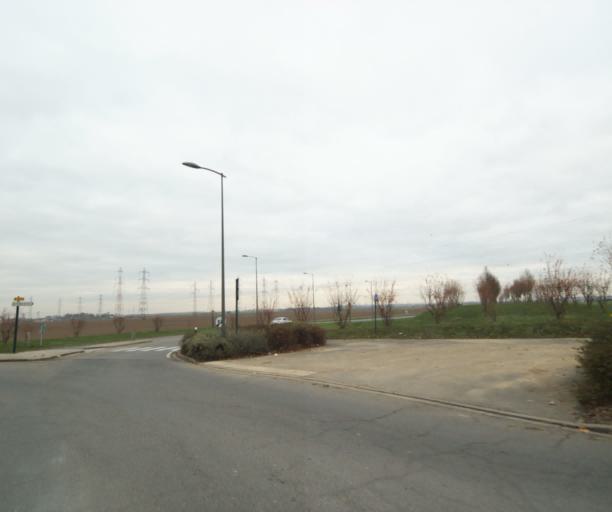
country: FR
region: Ile-de-France
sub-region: Departement du Val-d'Oise
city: Villiers-le-Bel
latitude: 49.0147
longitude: 2.4093
